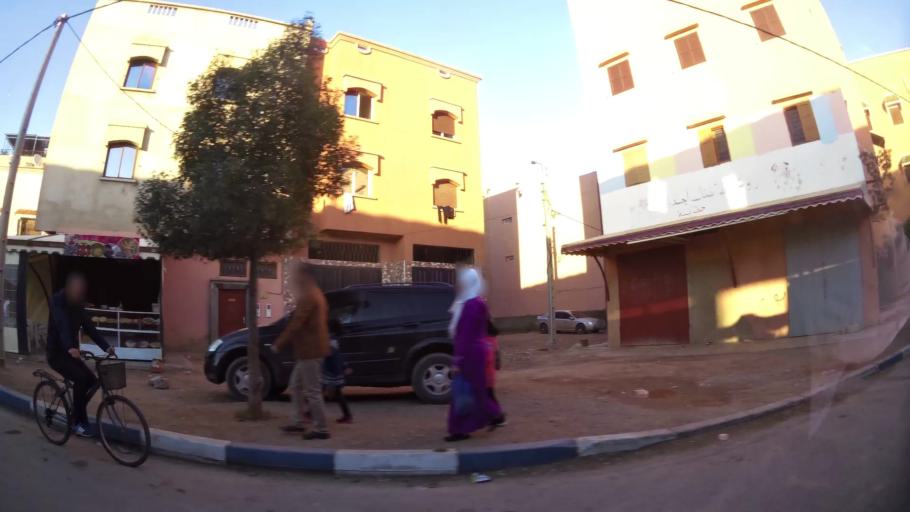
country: MA
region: Marrakech-Tensift-Al Haouz
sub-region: Kelaa-Des-Sraghna
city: Sidi Abdallah
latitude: 32.2404
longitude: -7.9535
